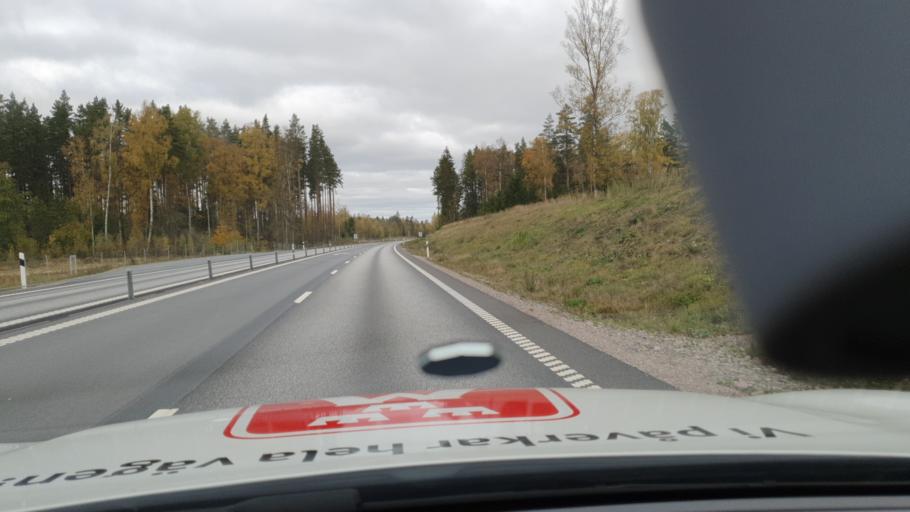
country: SE
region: OErebro
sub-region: Hallsbergs Kommun
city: Palsboda
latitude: 59.0869
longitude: 15.3077
